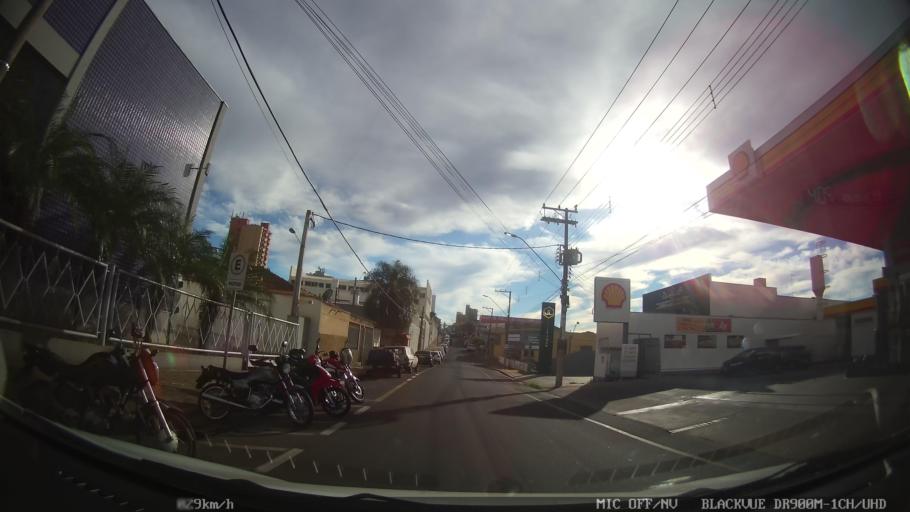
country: BR
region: Sao Paulo
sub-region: Catanduva
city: Catanduva
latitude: -21.1461
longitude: -48.9765
